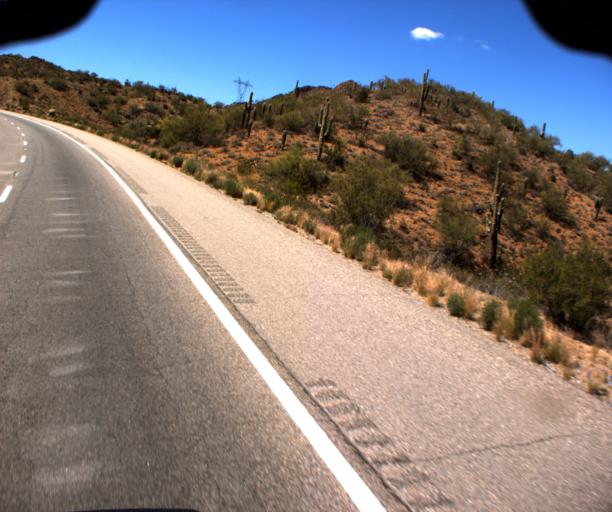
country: US
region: Arizona
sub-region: Yavapai County
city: Bagdad
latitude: 34.4561
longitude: -113.2897
